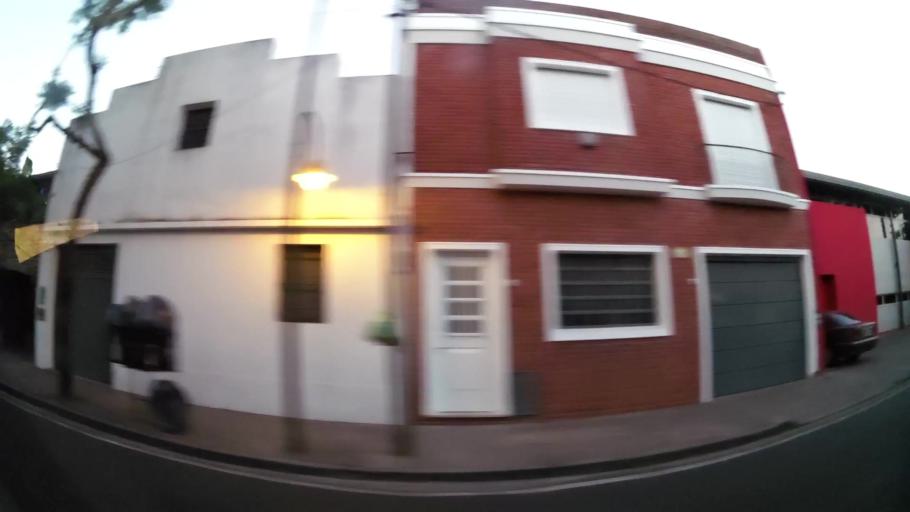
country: AR
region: Buenos Aires
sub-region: Partido de Tigre
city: Tigre
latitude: -34.4413
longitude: -58.5531
